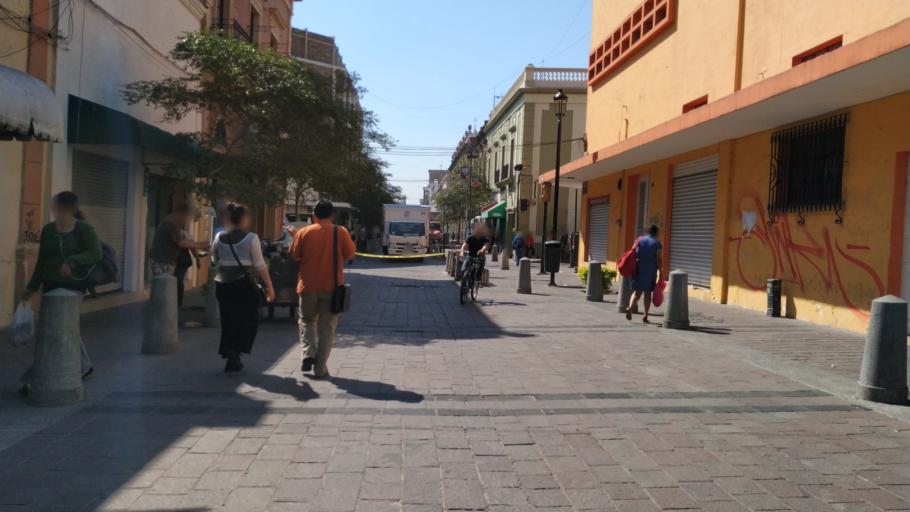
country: MX
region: Jalisco
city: Guadalajara
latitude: 20.6799
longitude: -103.3484
